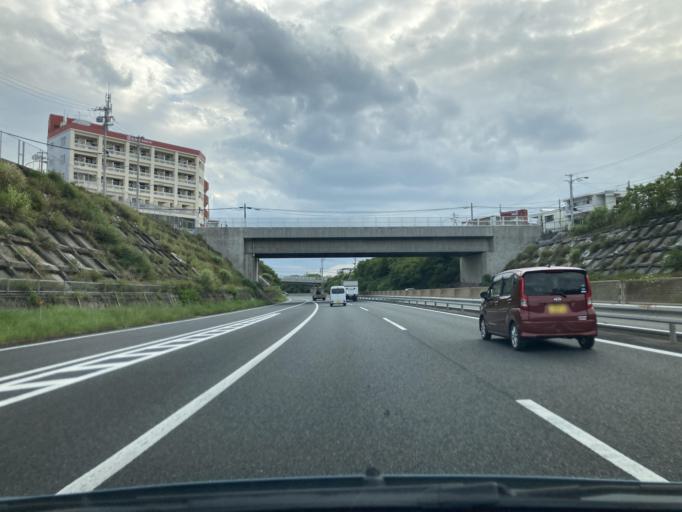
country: JP
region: Okinawa
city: Ginowan
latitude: 26.2556
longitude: 127.7637
